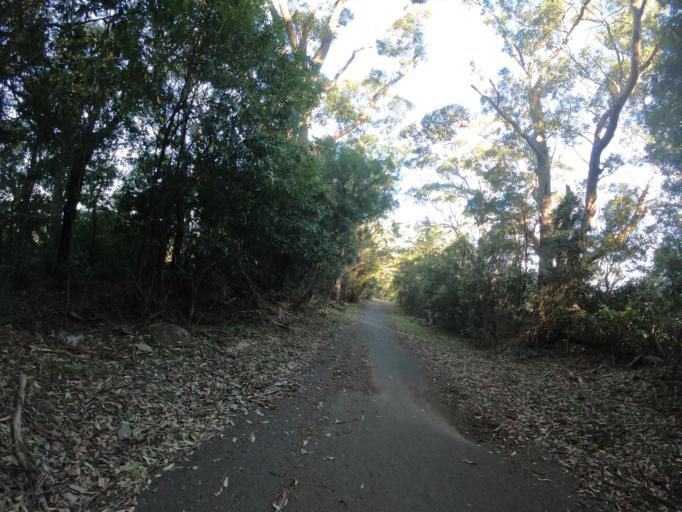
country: AU
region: New South Wales
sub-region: Wollongong
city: Mount Keira
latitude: -34.4121
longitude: 150.8356
